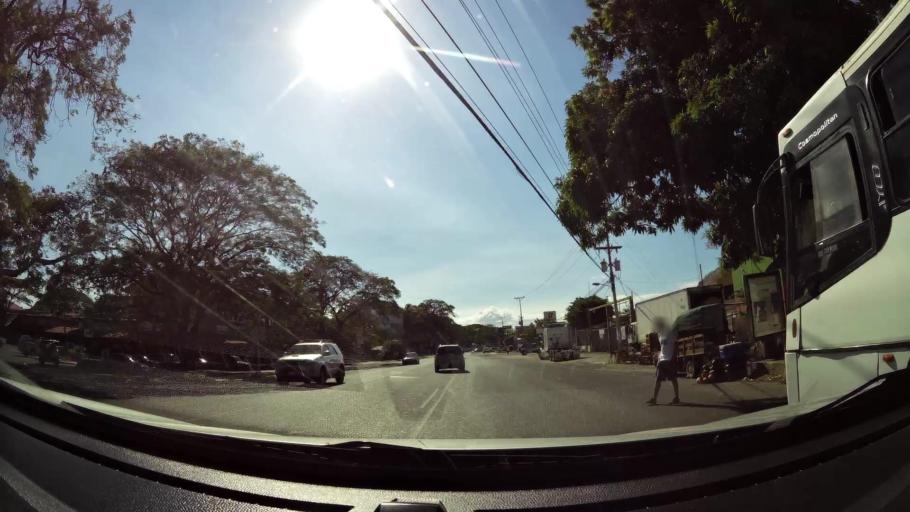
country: CR
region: Guanacaste
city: Liberia
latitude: 10.6264
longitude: -85.4446
